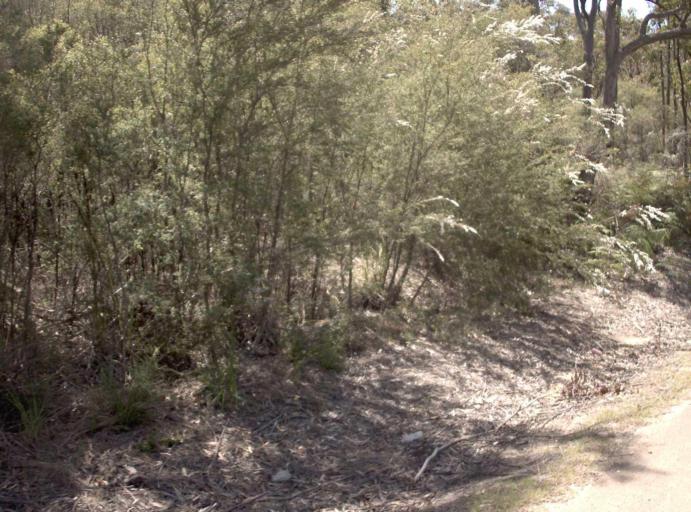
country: AU
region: Victoria
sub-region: East Gippsland
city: Lakes Entrance
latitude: -37.6603
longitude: 148.8025
